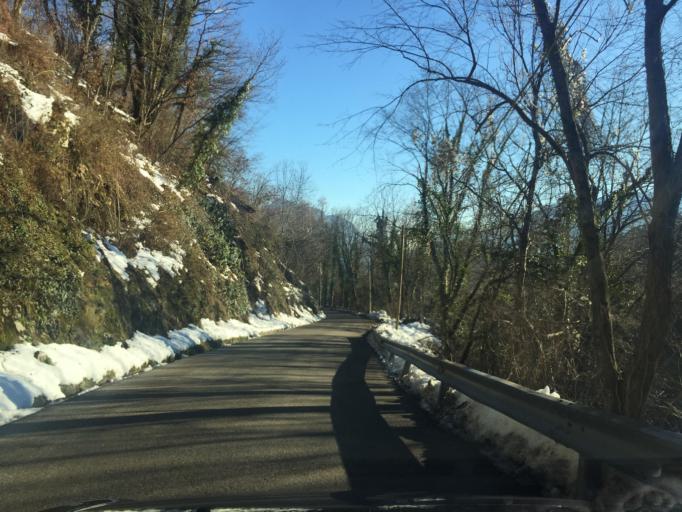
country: IT
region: Friuli Venezia Giulia
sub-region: Provincia di Udine
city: Chiaulis
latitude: 46.4211
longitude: 12.9953
